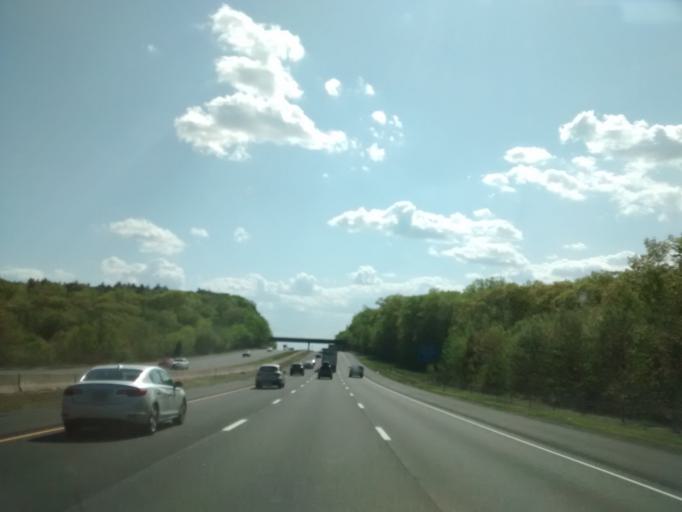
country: US
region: Connecticut
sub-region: Tolland County
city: Stafford
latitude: 41.9404
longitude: -72.2250
